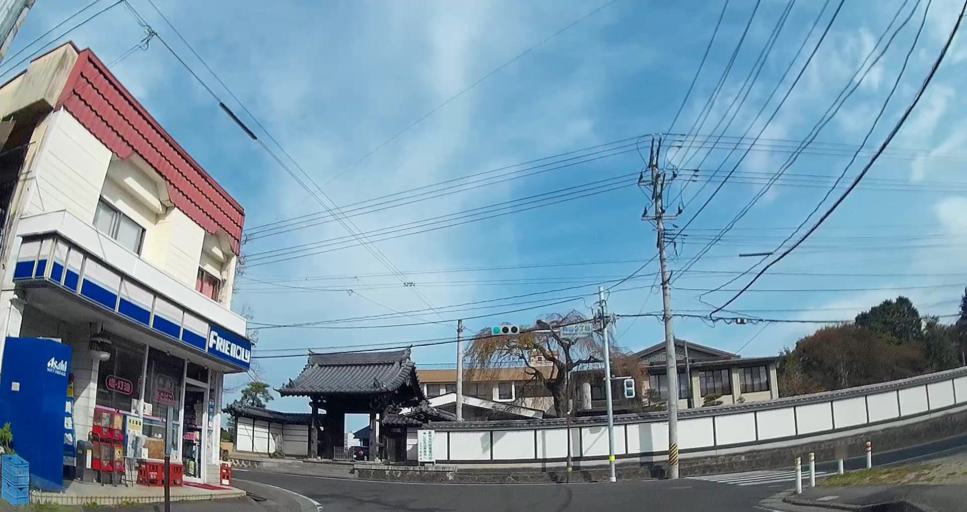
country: JP
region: Miyagi
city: Sendai
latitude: 38.2456
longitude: 140.8710
